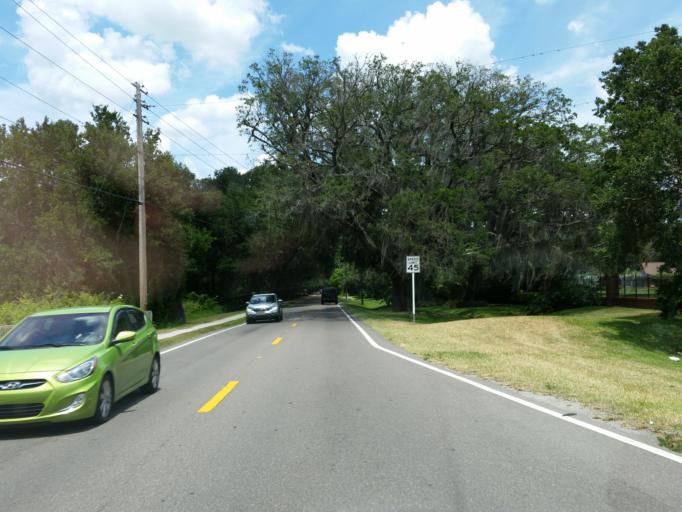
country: US
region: Florida
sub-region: Hillsborough County
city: Valrico
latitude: 27.9550
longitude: -82.2528
